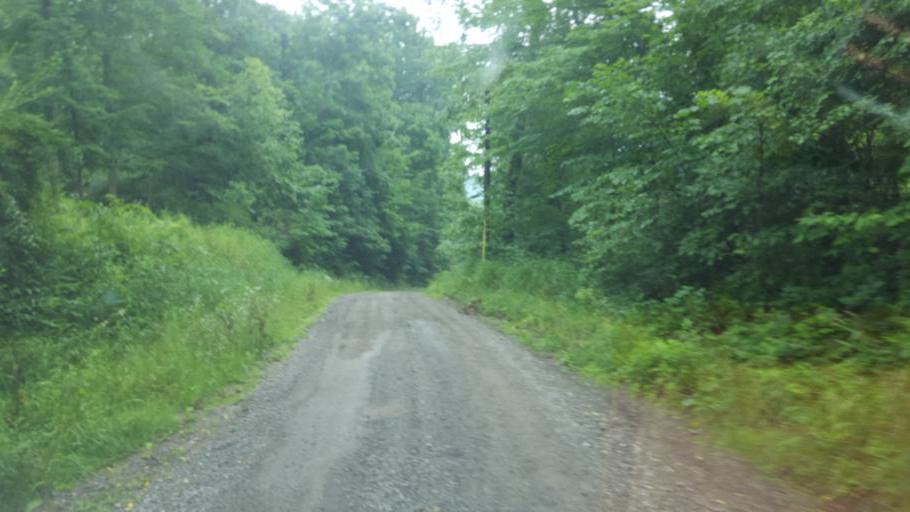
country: US
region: Ohio
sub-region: Columbiana County
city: Salineville
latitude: 40.5316
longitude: -80.8030
